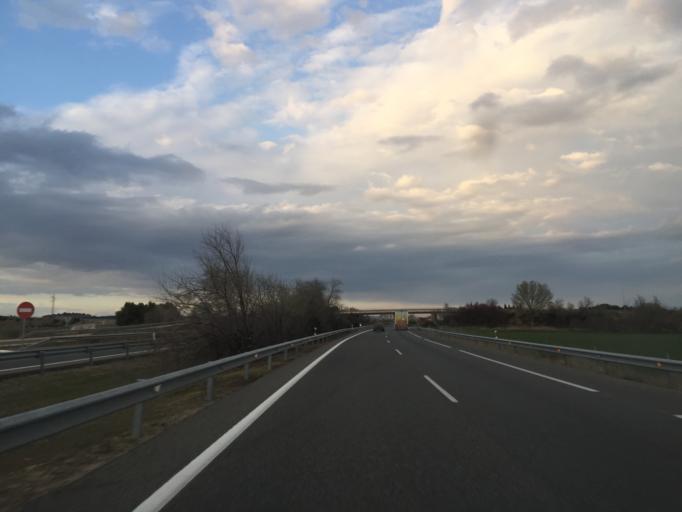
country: ES
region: Castille and Leon
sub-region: Provincia de Palencia
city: Villodrigo
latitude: 42.1454
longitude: -4.1024
